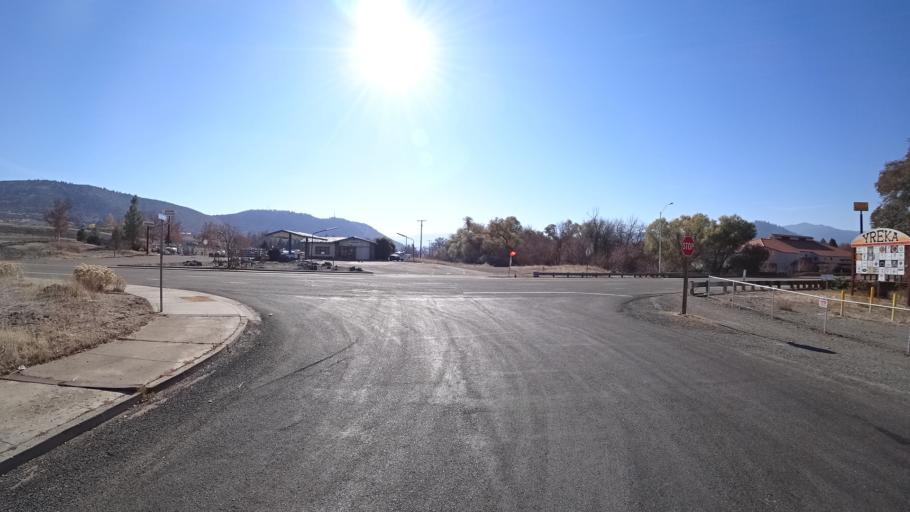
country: US
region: California
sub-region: Siskiyou County
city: Yreka
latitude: 41.7403
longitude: -122.6301
